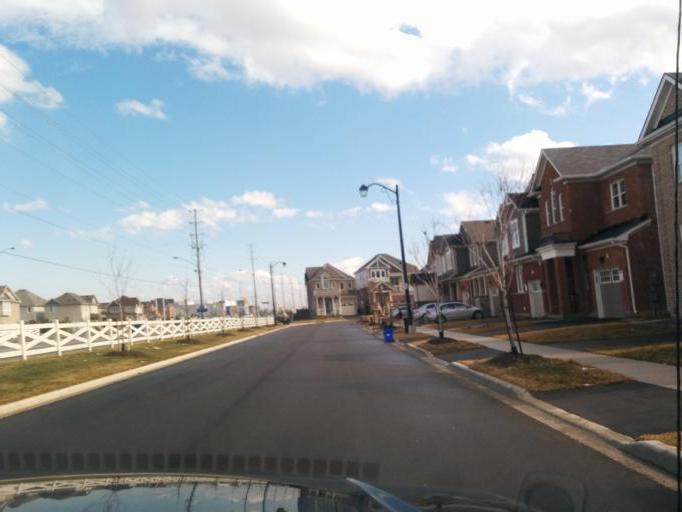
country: CA
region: Ontario
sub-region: Halton
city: Milton
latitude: 43.4893
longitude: -79.8627
